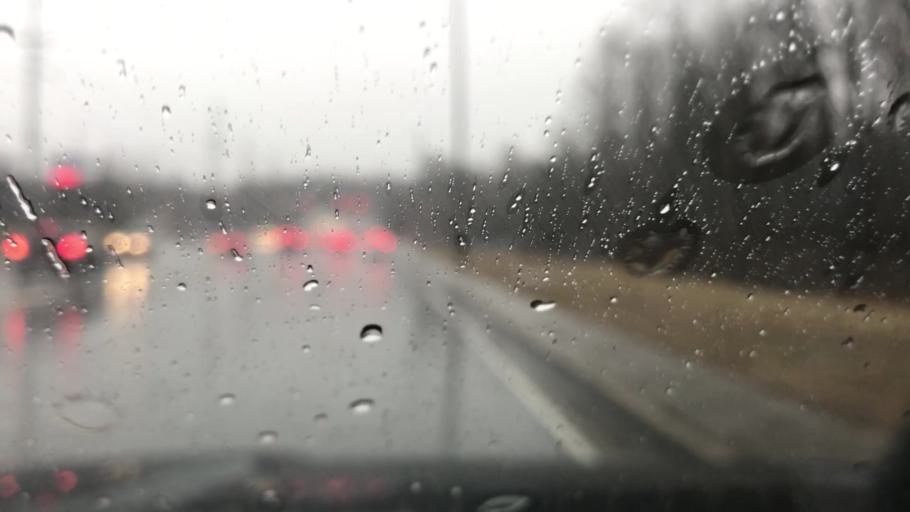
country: US
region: Tennessee
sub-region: Williamson County
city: Nolensville
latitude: 36.0460
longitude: -86.6757
